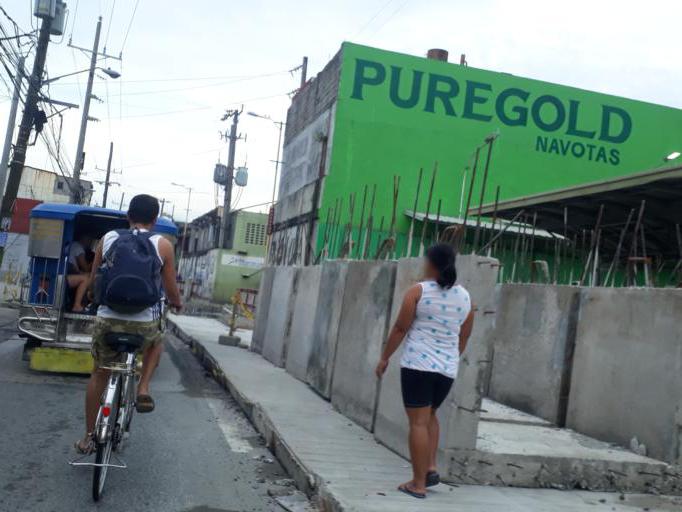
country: PH
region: Calabarzon
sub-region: Province of Rizal
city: Navotas
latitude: 14.6589
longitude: 120.9471
